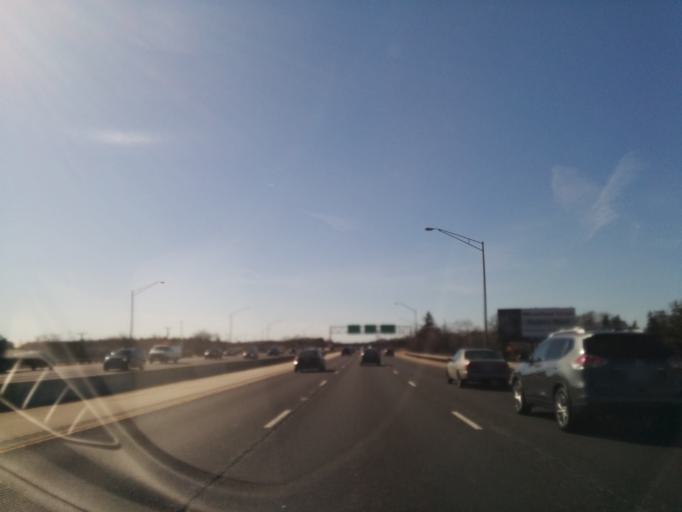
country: US
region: Illinois
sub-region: DuPage County
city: Darien
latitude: 41.7338
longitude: -87.9664
